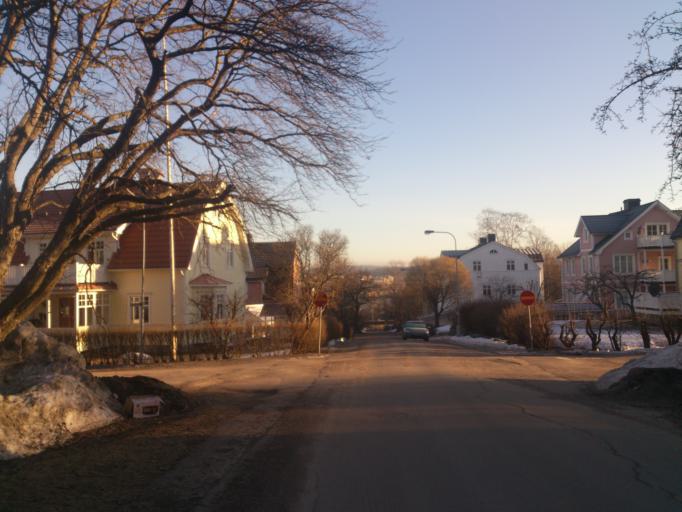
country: SE
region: Vaesternorrland
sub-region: Sundsvalls Kommun
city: Sundsvall
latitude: 62.3822
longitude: 17.3171
